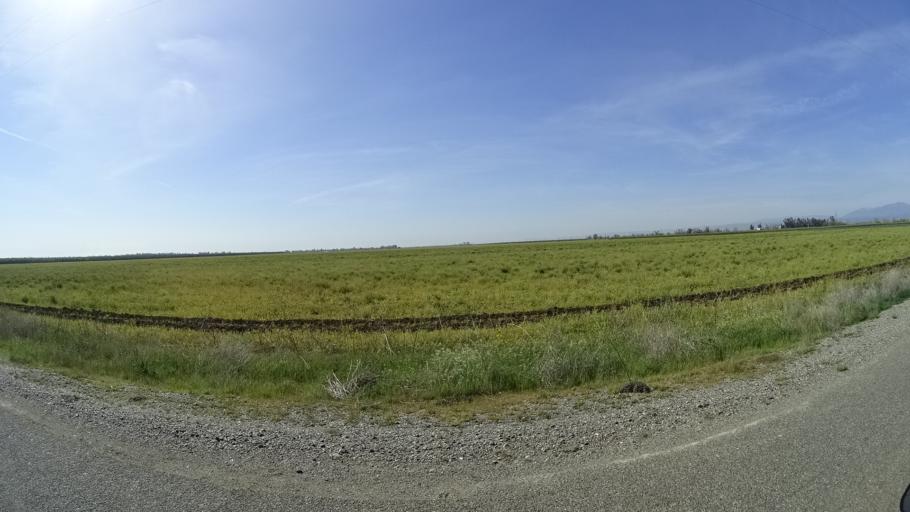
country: US
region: California
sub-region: Glenn County
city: Willows
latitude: 39.6114
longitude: -122.2285
